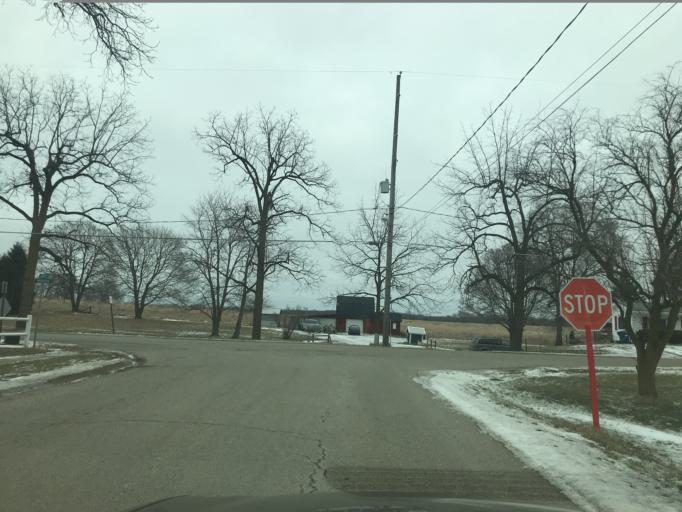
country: US
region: Michigan
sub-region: Jackson County
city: Brooklyn
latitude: 42.0699
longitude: -84.3264
